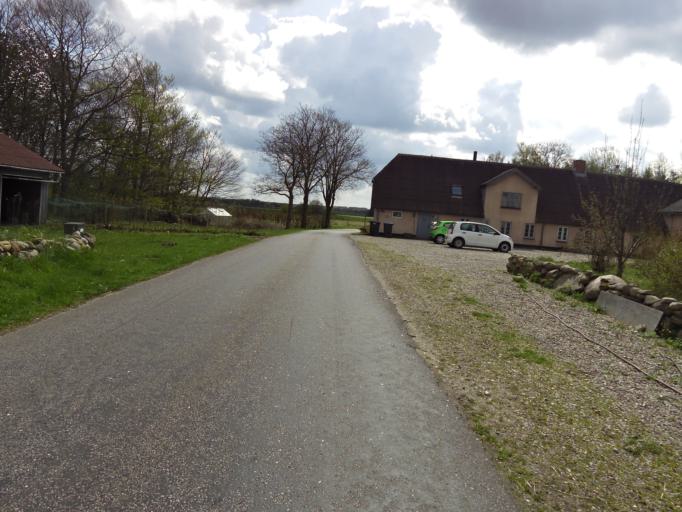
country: DK
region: South Denmark
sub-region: Tonder Kommune
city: Toftlund
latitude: 55.2044
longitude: 9.1643
